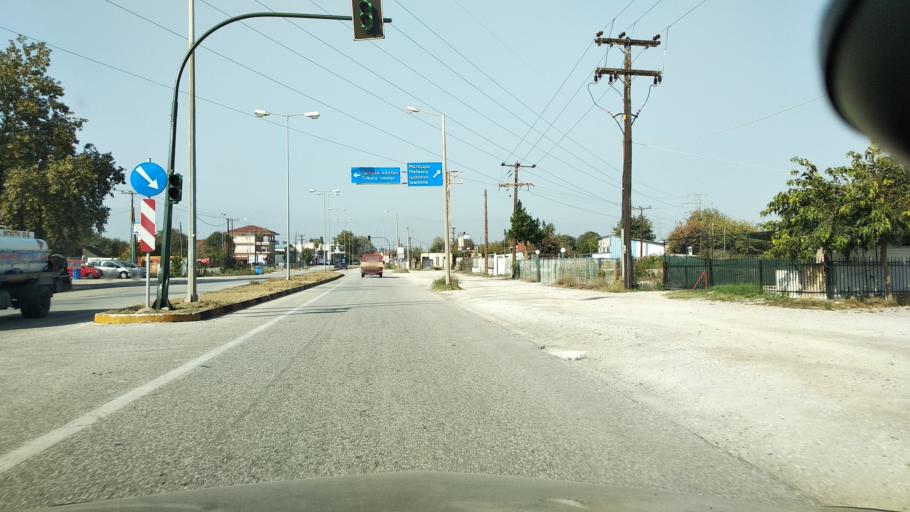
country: GR
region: Thessaly
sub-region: Trikala
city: Trikala
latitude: 39.5560
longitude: 21.7898
